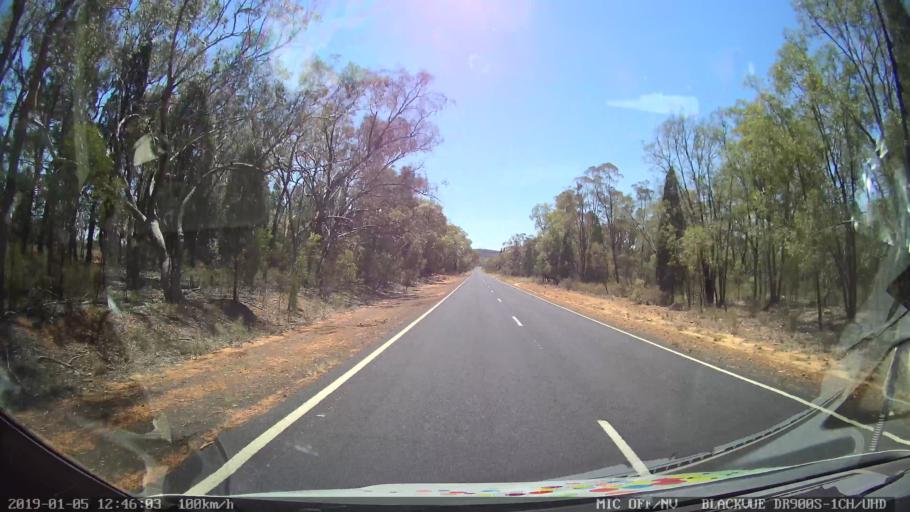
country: AU
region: New South Wales
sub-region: Warrumbungle Shire
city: Coonabarabran
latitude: -31.1219
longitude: 149.5575
